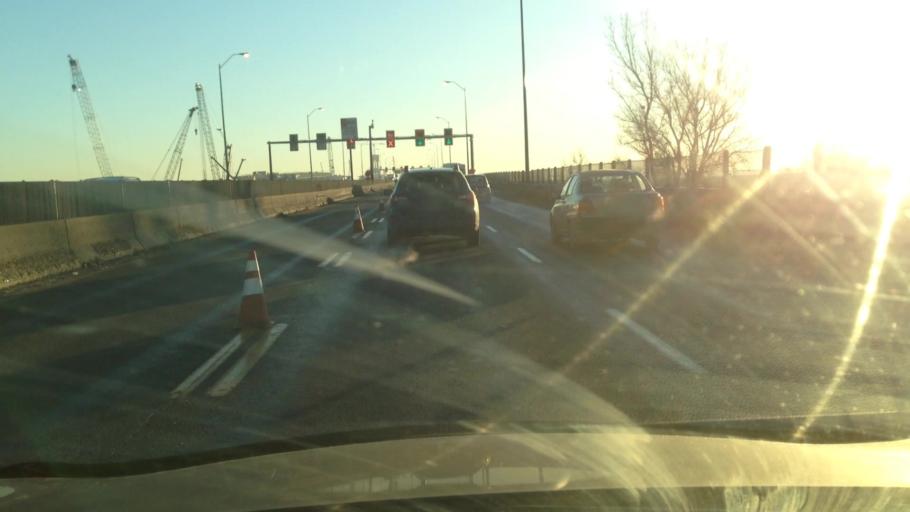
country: CA
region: Quebec
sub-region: Monteregie
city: Longueuil
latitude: 45.4698
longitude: -73.5352
